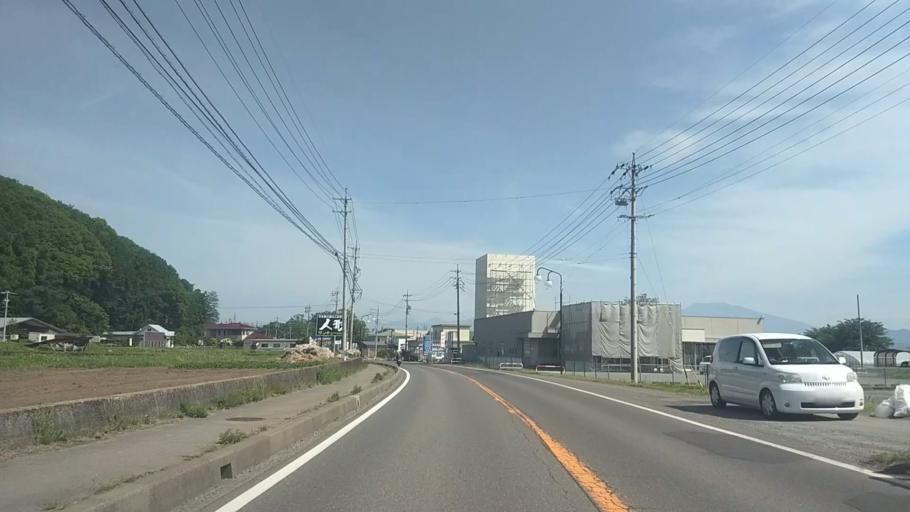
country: JP
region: Nagano
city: Saku
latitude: 36.1755
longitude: 138.4850
